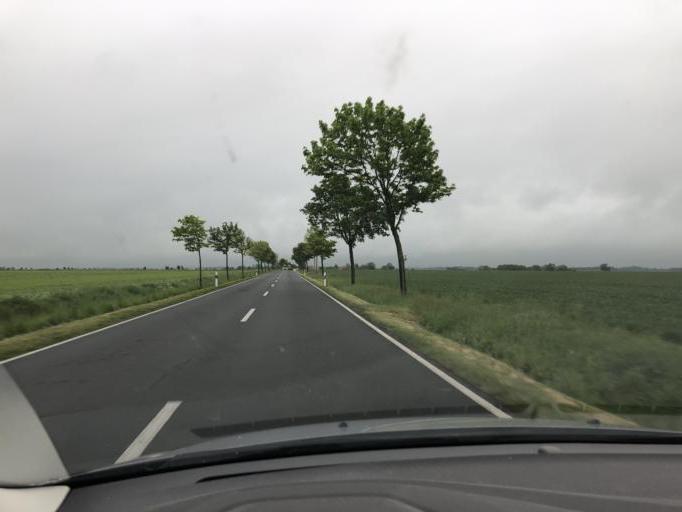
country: DE
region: Saxony
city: Zschortau
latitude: 51.4938
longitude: 12.4001
